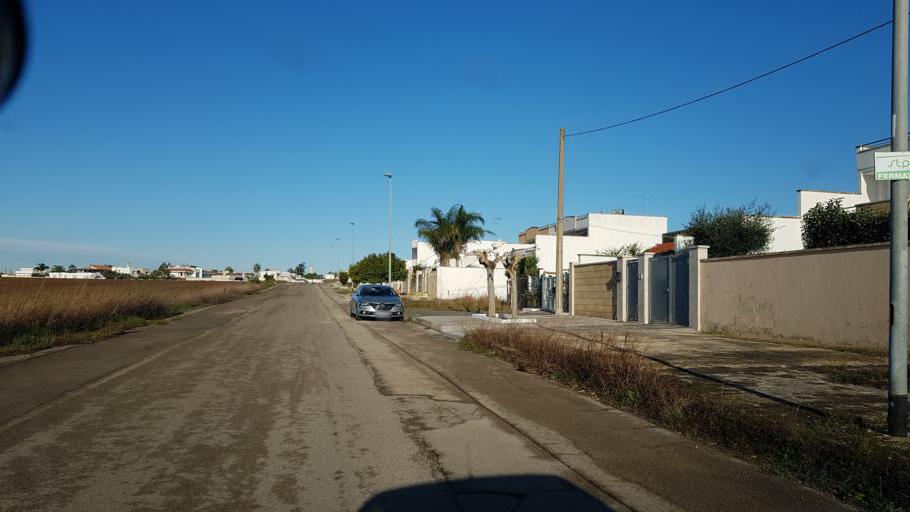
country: IT
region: Apulia
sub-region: Provincia di Brindisi
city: Torchiarolo
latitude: 40.5361
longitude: 18.0712
